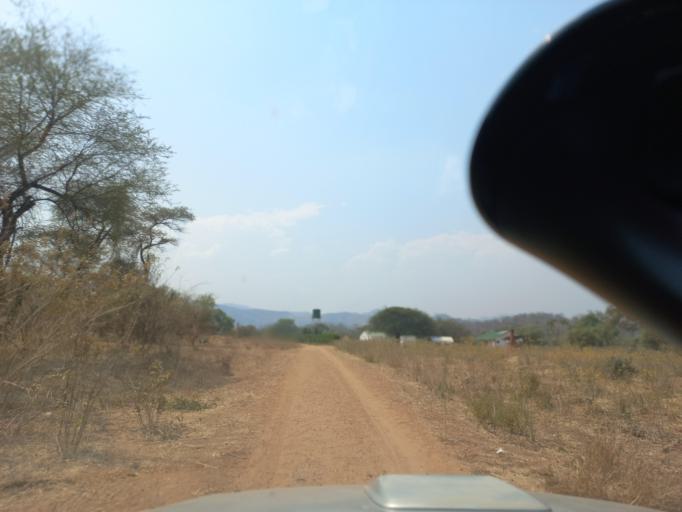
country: ZW
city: Chirundu
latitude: -15.9113
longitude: 28.6870
